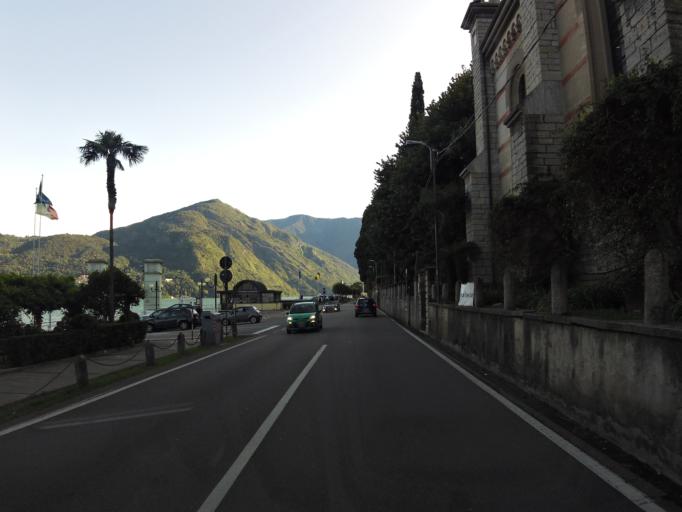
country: IT
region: Lombardy
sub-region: Provincia di Como
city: Cadenabbia
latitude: 45.9910
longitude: 9.2374
